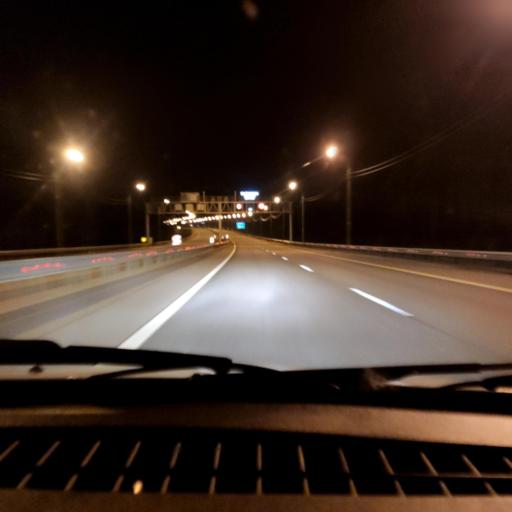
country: RU
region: Lipetsk
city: Khlevnoye
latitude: 52.3083
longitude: 39.0487
